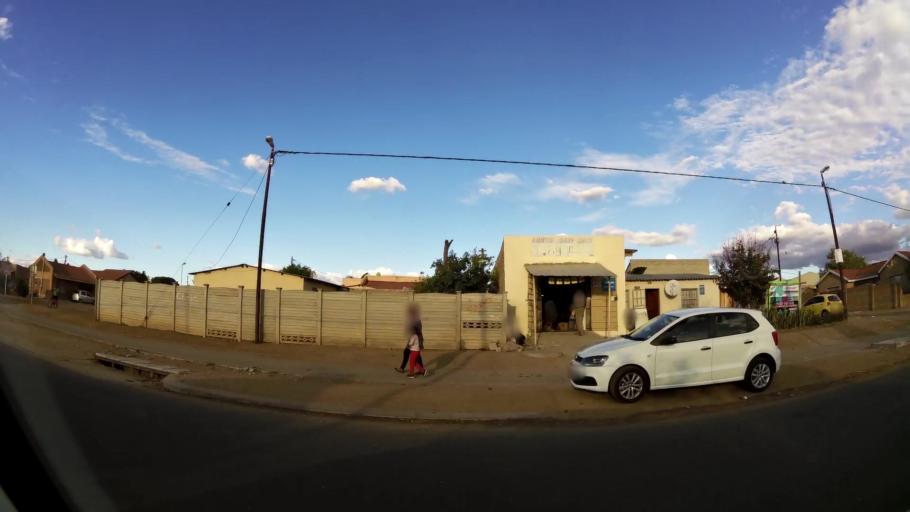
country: ZA
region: Limpopo
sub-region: Capricorn District Municipality
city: Polokwane
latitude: -23.9100
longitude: 29.4280
